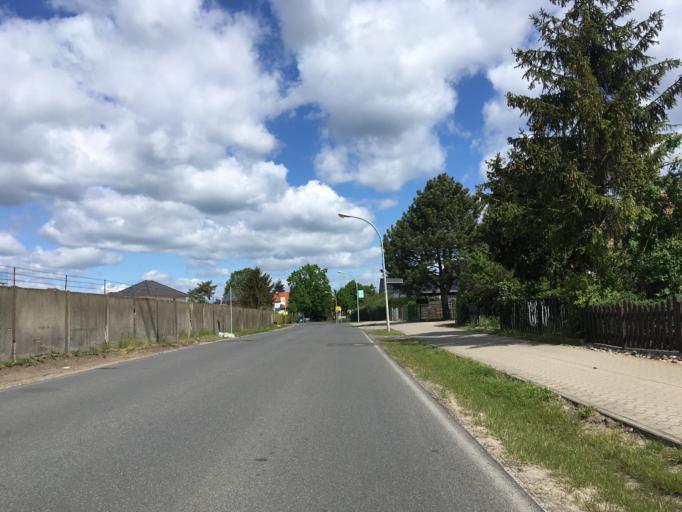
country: DE
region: Brandenburg
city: Oranienburg
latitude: 52.7675
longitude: 13.2522
